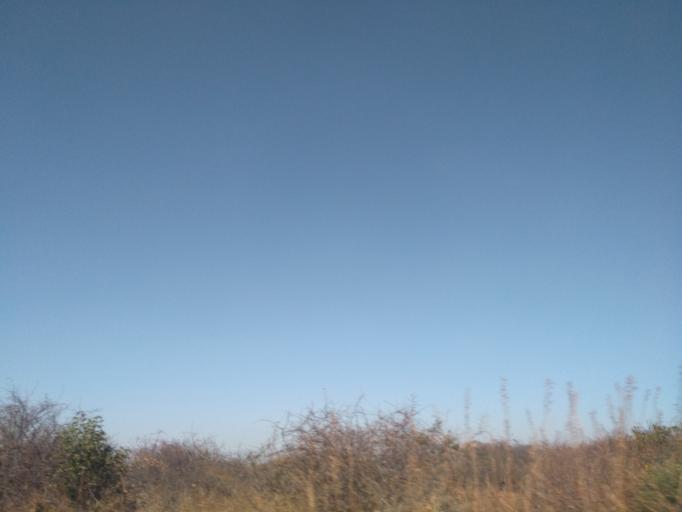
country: TZ
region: Dodoma
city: Dodoma
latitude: -6.1739
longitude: 35.7010
